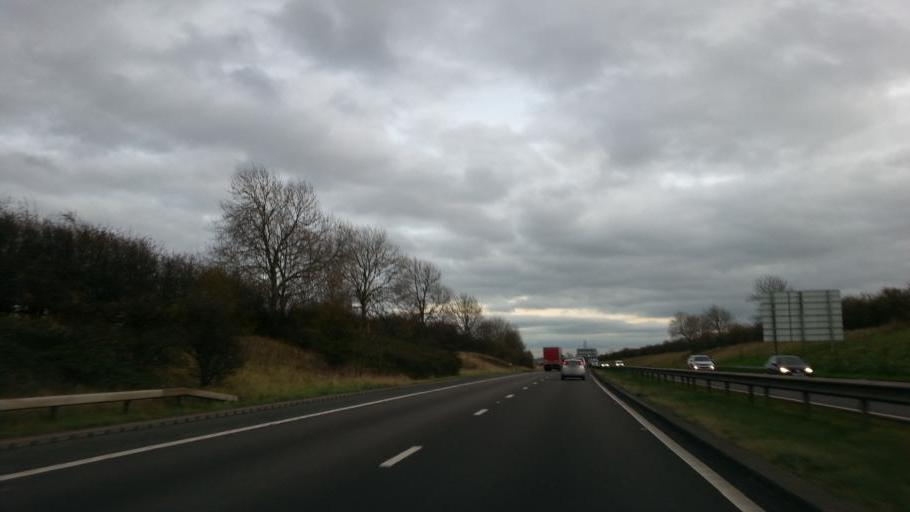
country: GB
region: England
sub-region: Doncaster
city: Tickhill
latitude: 53.4636
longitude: -1.1295
